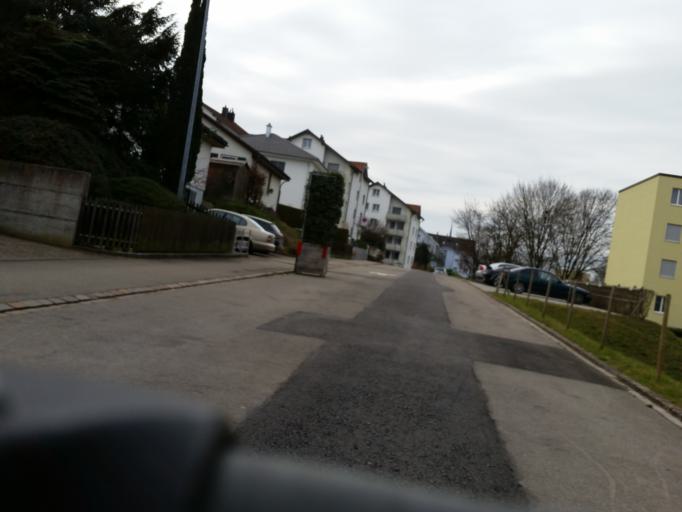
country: CH
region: Thurgau
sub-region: Arbon District
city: Amriswil
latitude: 47.5436
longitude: 9.3102
